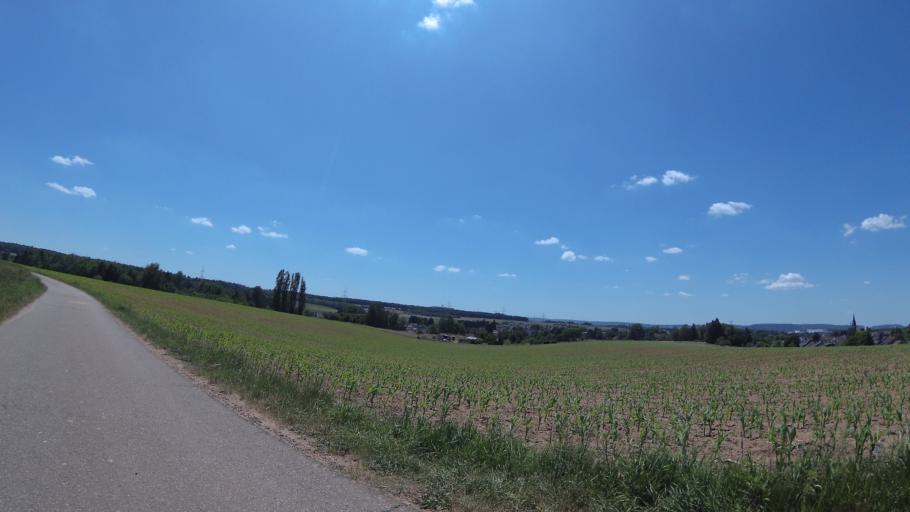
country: DE
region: Saarland
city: Saarwellingen
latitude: 49.3545
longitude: 6.8225
